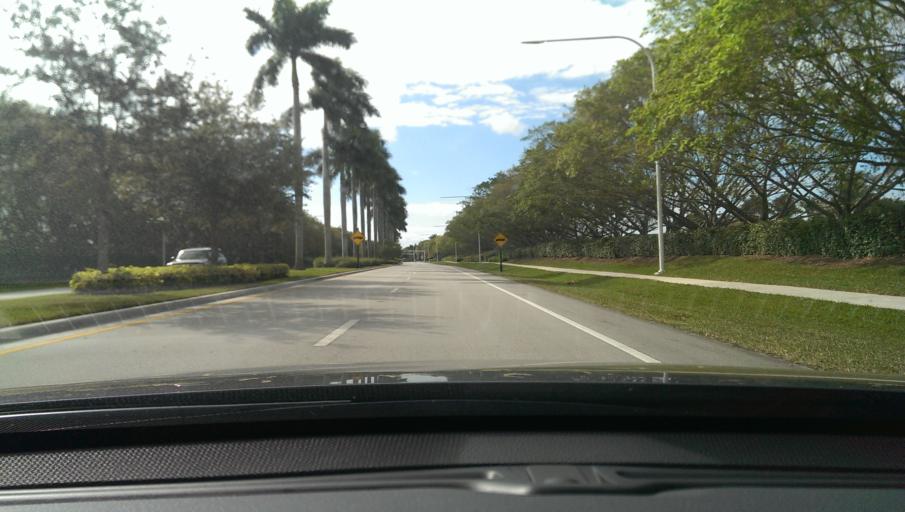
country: US
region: Florida
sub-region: Broward County
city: Weston
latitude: 26.0733
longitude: -80.3935
